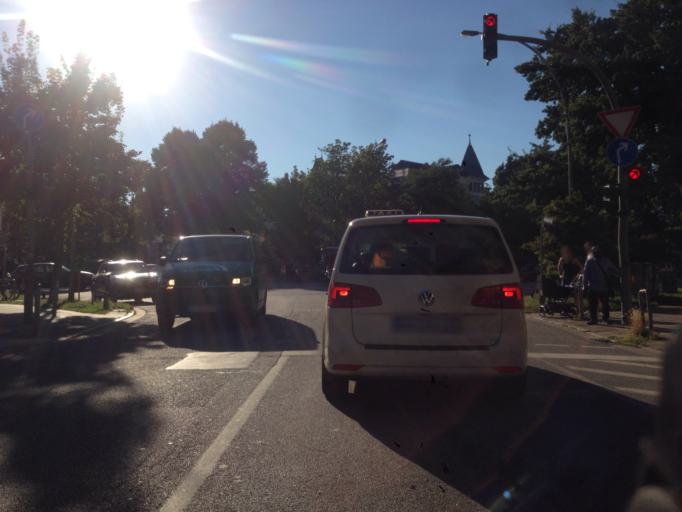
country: DE
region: Hamburg
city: Hamburg
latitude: 53.5781
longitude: 10.0149
